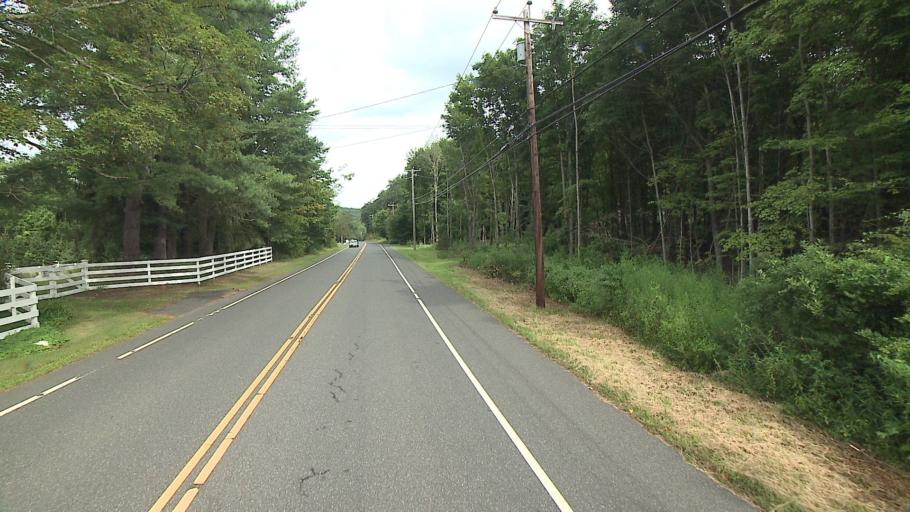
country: US
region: Connecticut
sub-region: Litchfield County
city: Woodbury
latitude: 41.5807
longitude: -73.2451
